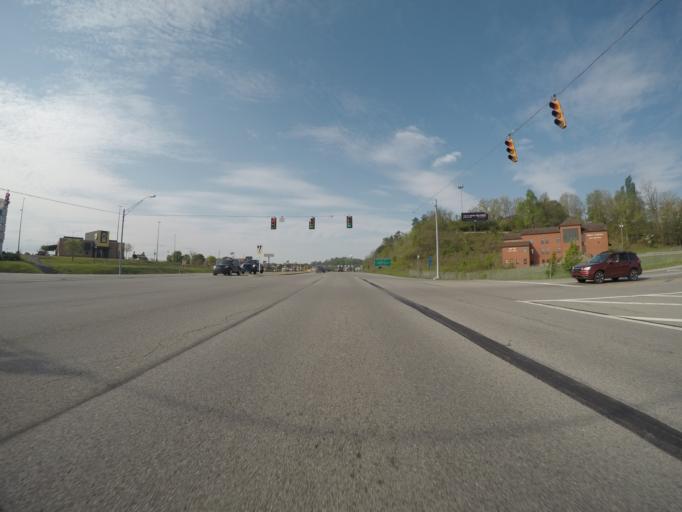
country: US
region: West Virginia
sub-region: Kanawha County
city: Dunbar
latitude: 38.3238
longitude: -81.7157
